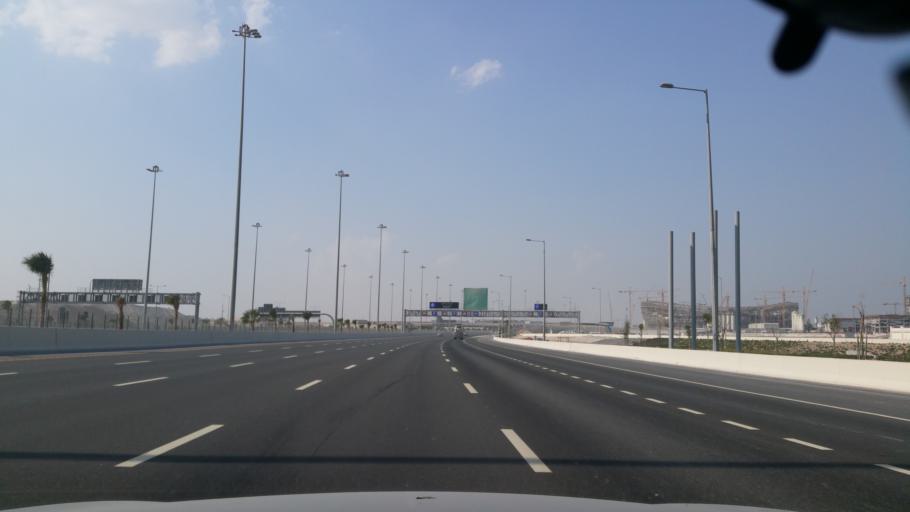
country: QA
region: Baladiyat Umm Salal
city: Umm Salal Muhammad
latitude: 25.4054
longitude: 51.4910
